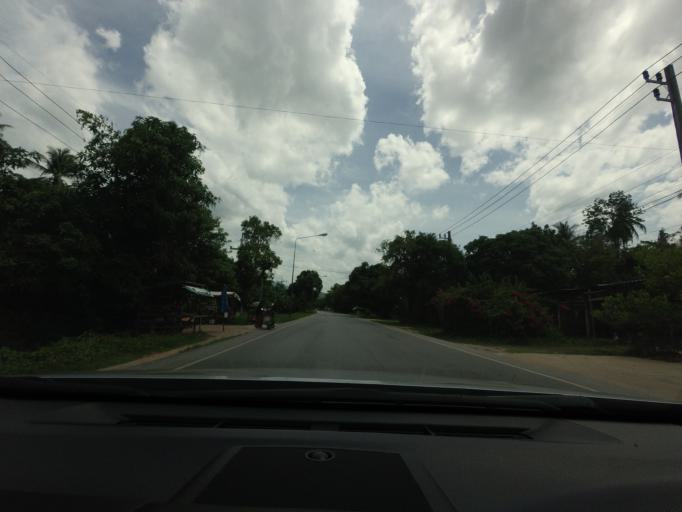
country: TH
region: Yala
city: Raman
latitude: 6.4612
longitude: 101.3701
